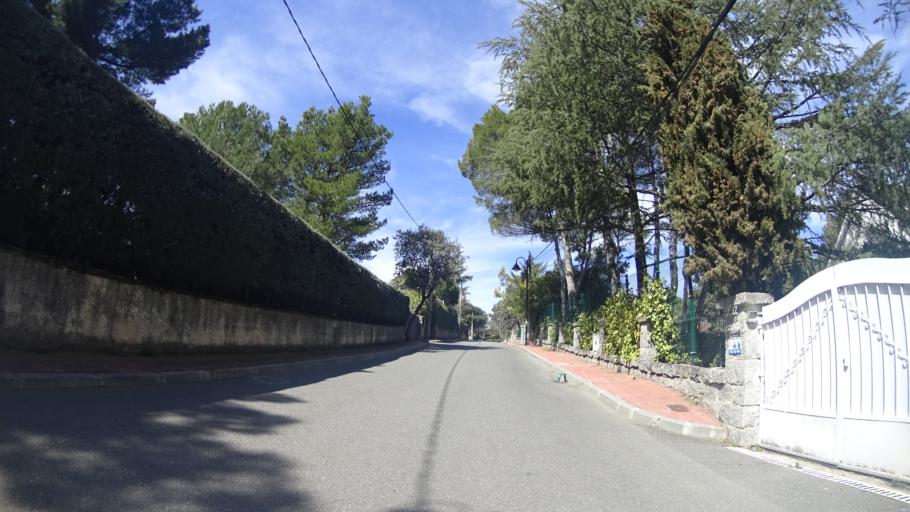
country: ES
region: Madrid
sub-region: Provincia de Madrid
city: Galapagar
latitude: 40.5921
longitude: -3.9835
